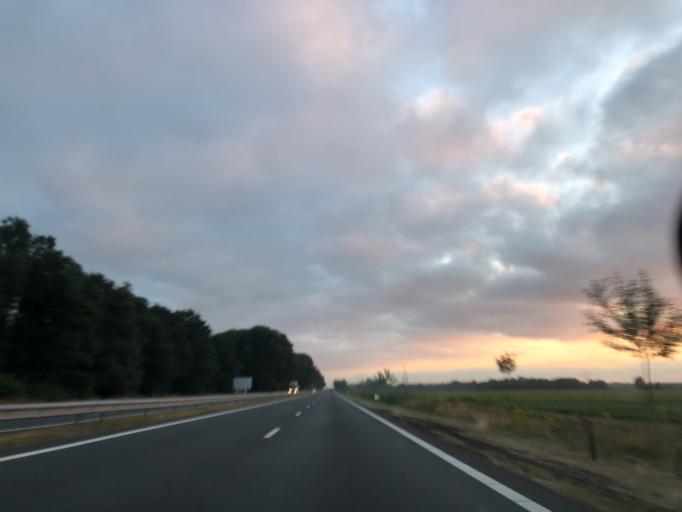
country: NL
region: Groningen
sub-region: Gemeente Veendam
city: Veendam
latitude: 53.1118
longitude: 6.8995
